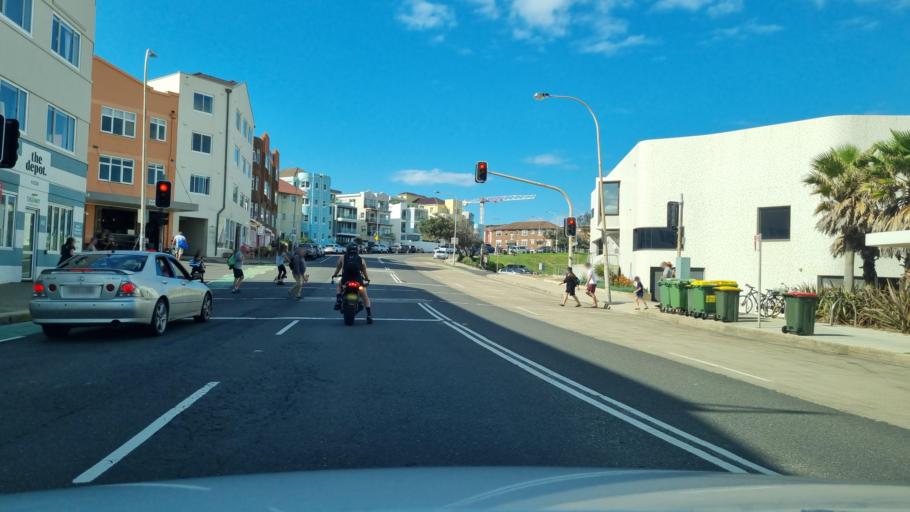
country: AU
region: New South Wales
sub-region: Waverley
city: North Bondi
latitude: -33.8898
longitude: 151.2806
